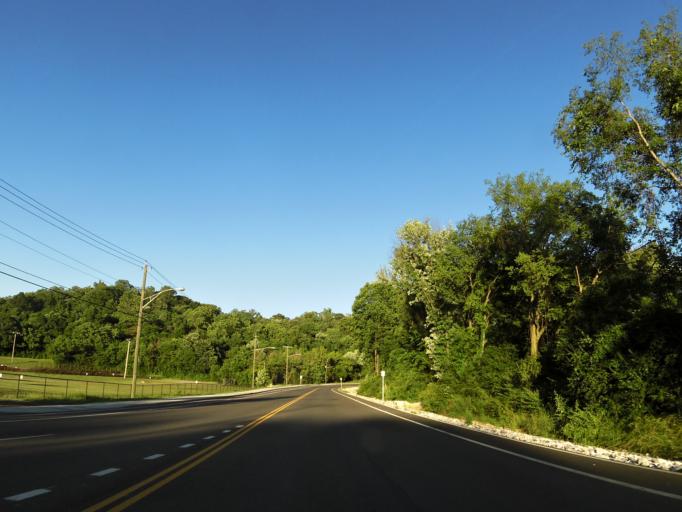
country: US
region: Tennessee
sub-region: Knox County
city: Knoxville
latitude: 36.0022
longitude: -83.8820
